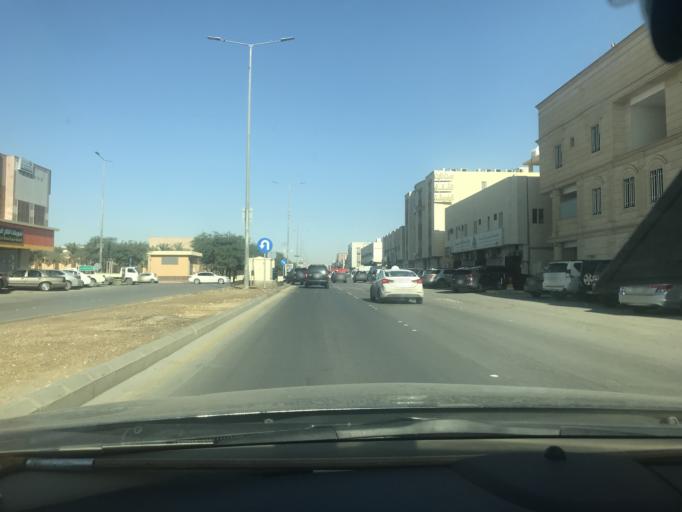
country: SA
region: Ar Riyad
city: Riyadh
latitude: 24.7530
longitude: 46.6695
